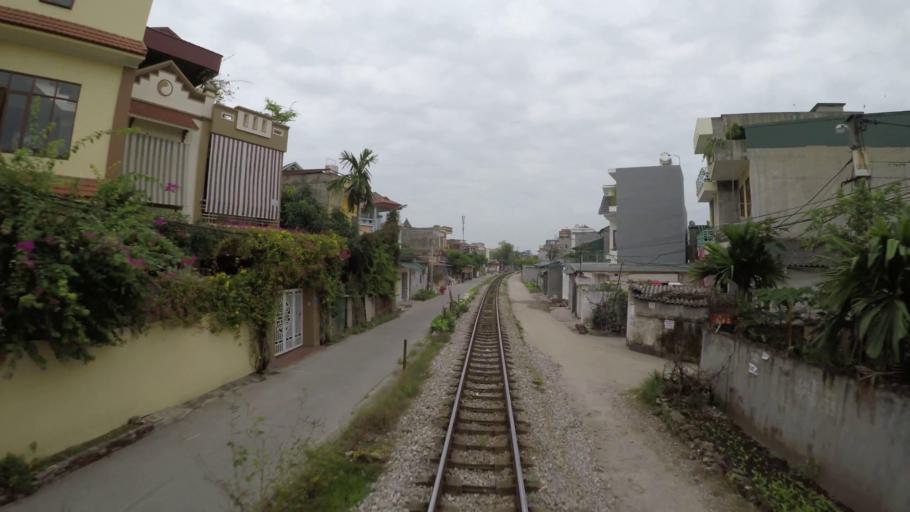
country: VN
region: Hai Duong
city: Lai Cach
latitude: 20.9434
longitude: 106.2871
